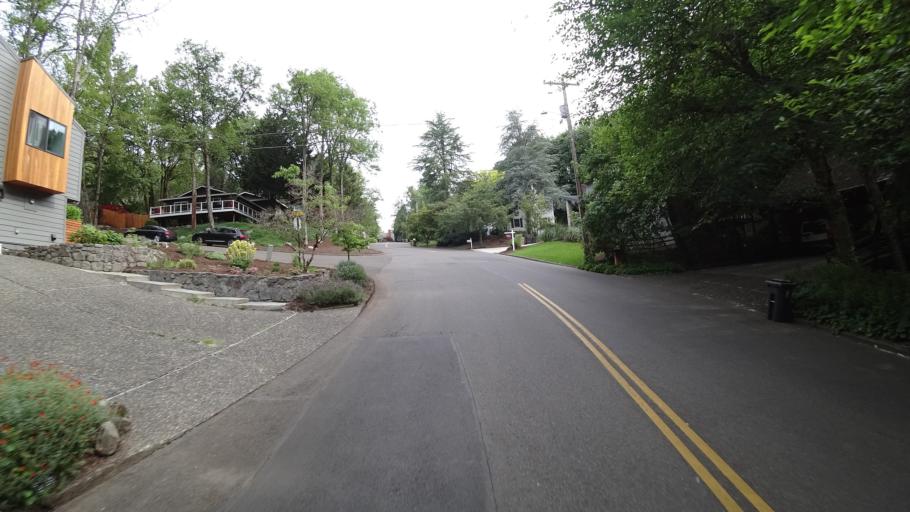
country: US
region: Oregon
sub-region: Clackamas County
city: Lake Oswego
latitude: 45.4289
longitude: -122.6805
